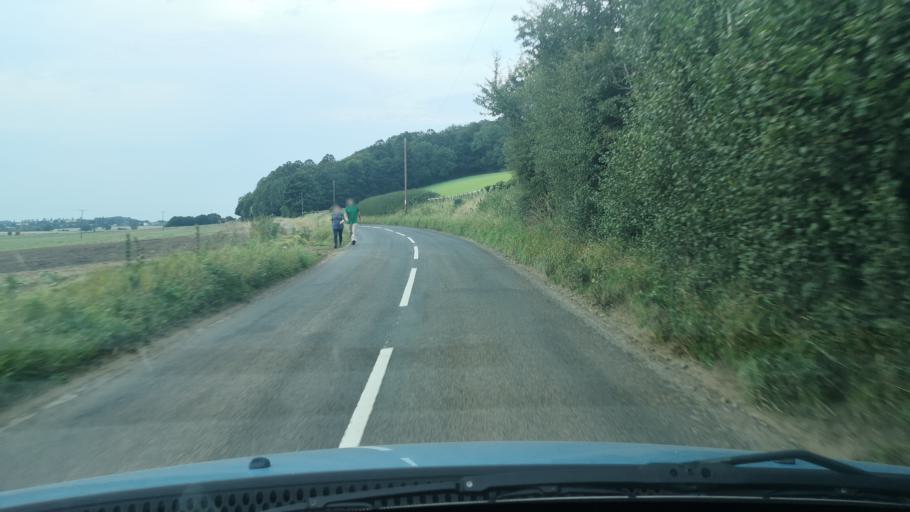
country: GB
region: England
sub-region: City and Borough of Wakefield
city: Darrington
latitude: 53.6528
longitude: -1.2680
